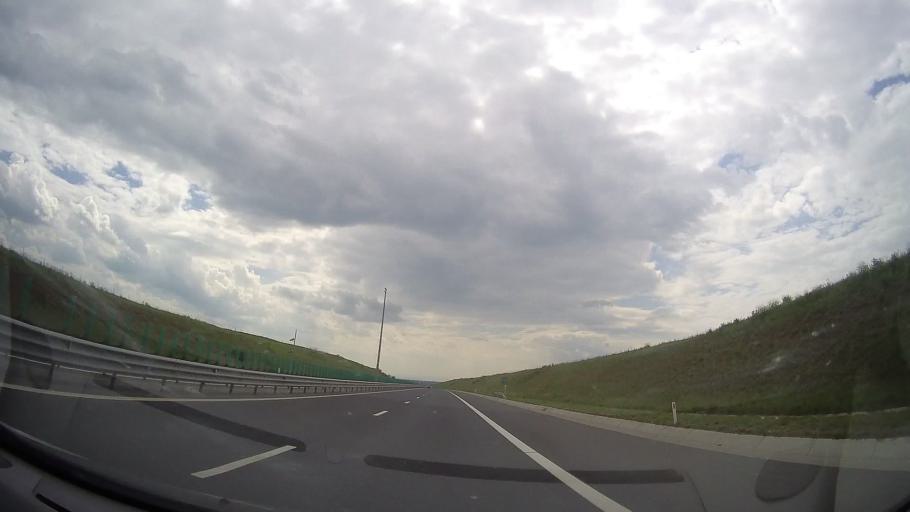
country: RO
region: Alba
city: Vurpar
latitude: 45.9598
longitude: 23.4477
